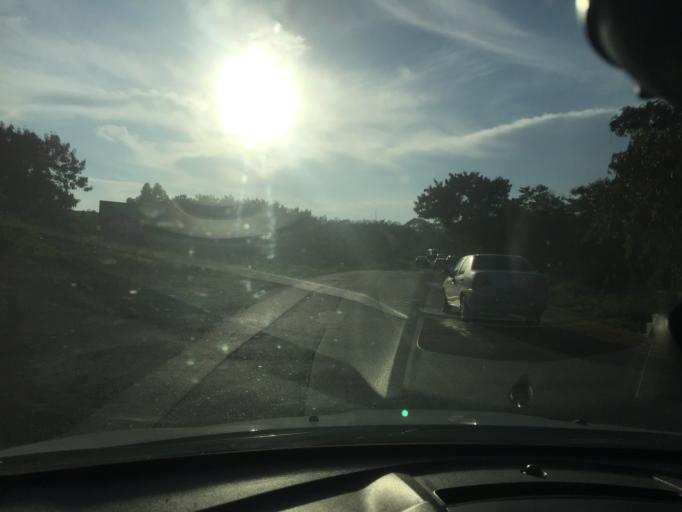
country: BR
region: Sao Paulo
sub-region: Varzea Paulista
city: Varzea Paulista
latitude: -23.2083
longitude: -46.8294
